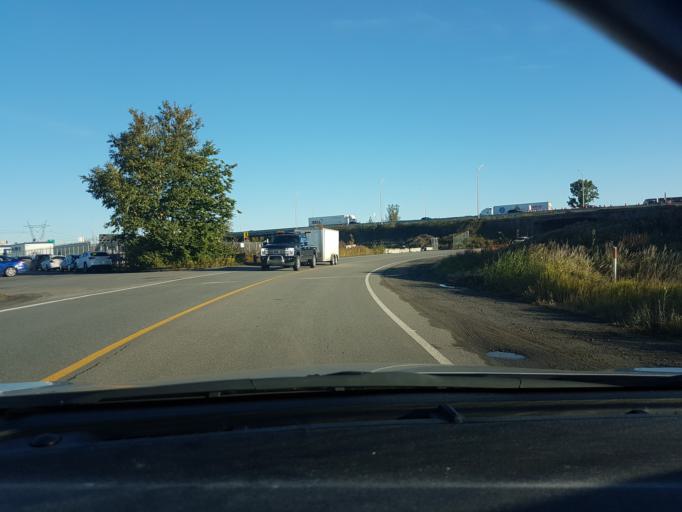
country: CA
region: Quebec
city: L'Ancienne-Lorette
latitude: 46.7951
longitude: -71.3191
